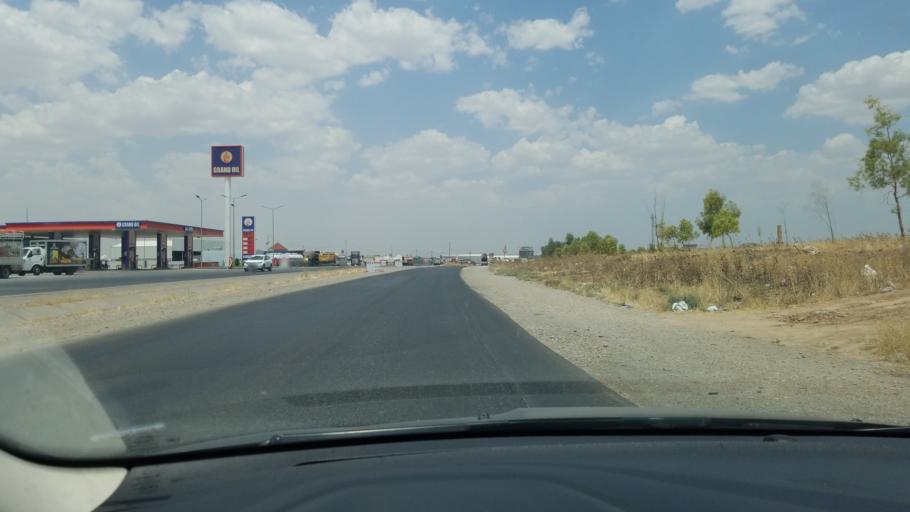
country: IQ
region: Arbil
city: Erbil
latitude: 36.0925
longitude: 44.0227
